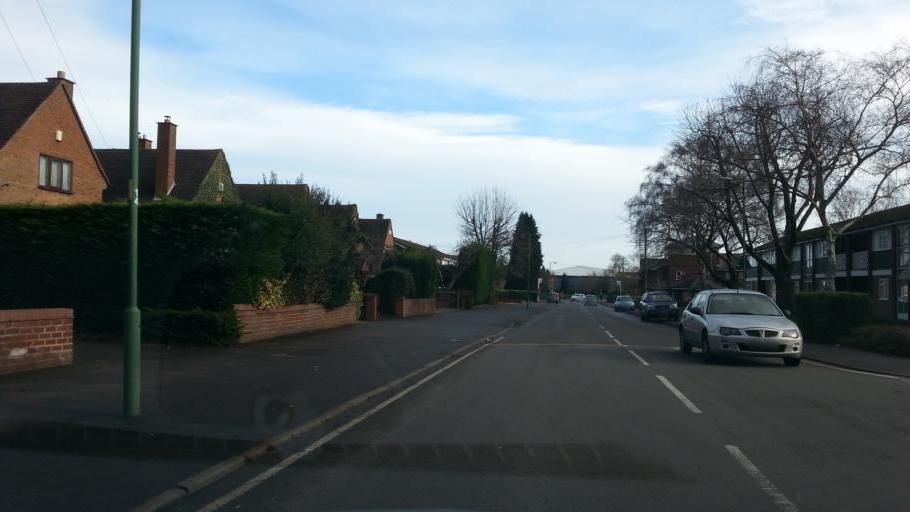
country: GB
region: England
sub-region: City and Borough of Birmingham
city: Acocks Green
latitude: 52.4443
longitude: -1.7903
